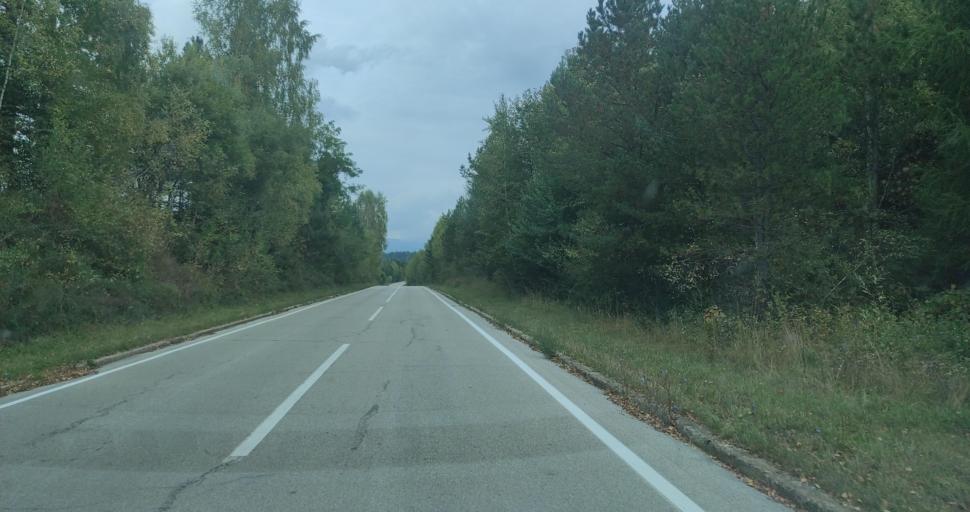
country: RS
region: Central Serbia
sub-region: Jablanicki Okrug
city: Crna Trava
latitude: 42.6871
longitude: 22.3159
